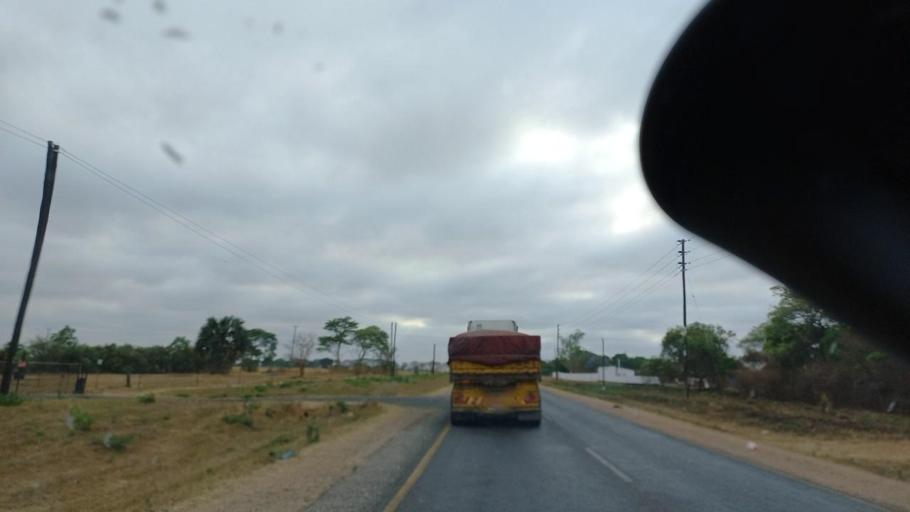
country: ZM
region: Lusaka
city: Chongwe
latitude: -15.3508
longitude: 28.5603
